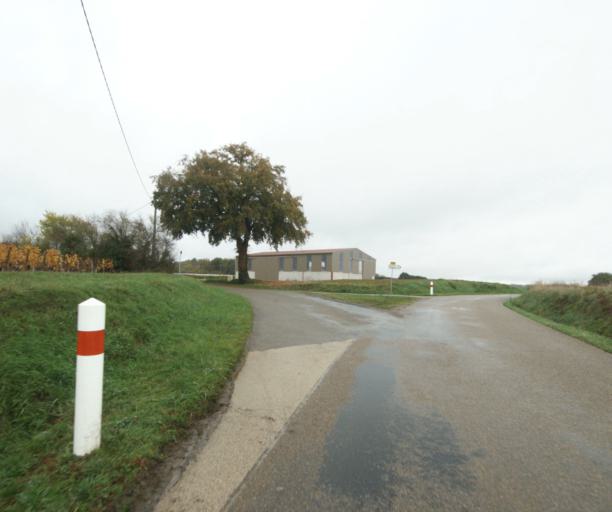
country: FR
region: Rhone-Alpes
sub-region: Departement de l'Ain
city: Pont-de-Vaux
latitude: 46.4786
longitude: 4.8599
